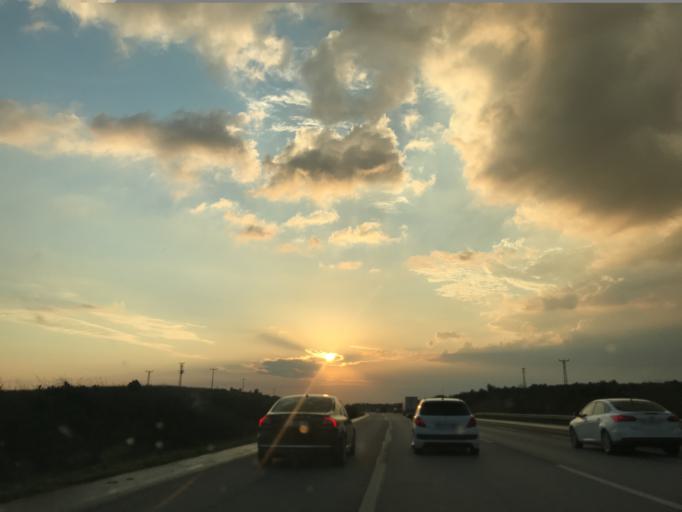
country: TR
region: Mersin
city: Yenice
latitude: 37.0371
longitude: 35.1348
